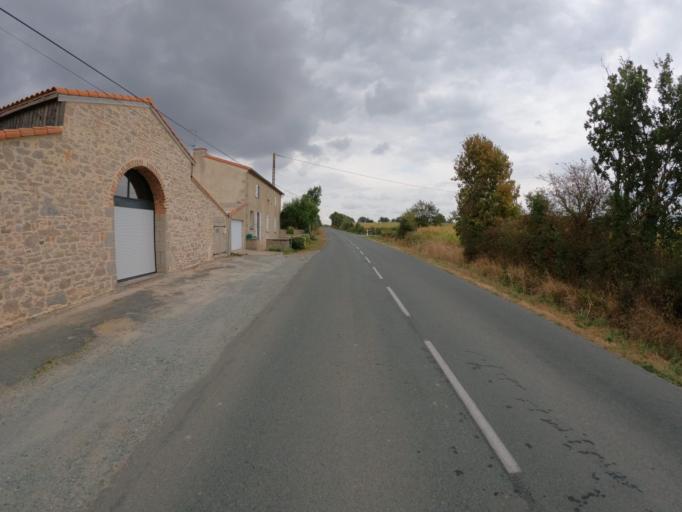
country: FR
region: Pays de la Loire
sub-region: Departement de la Vendee
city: Tiffauges
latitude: 46.9953
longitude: -1.0912
